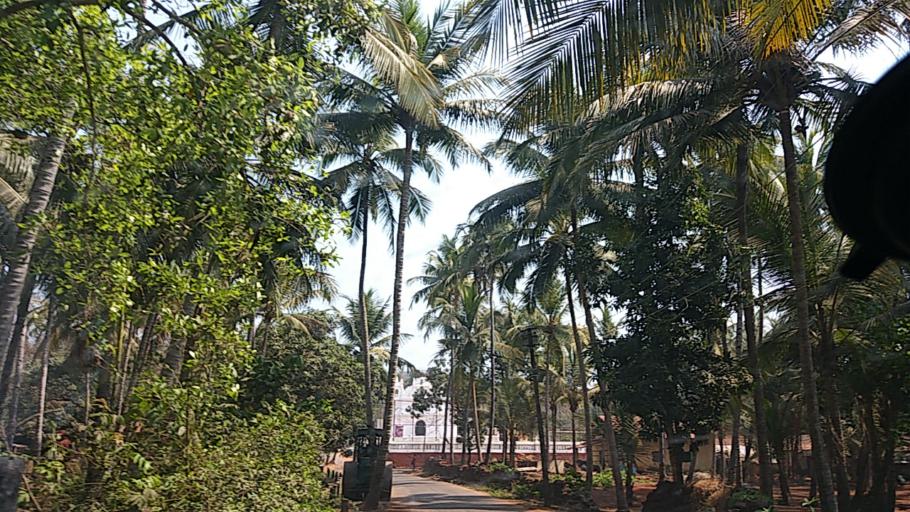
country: IN
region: Goa
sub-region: South Goa
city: Sancoale
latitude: 15.3731
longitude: 73.9150
